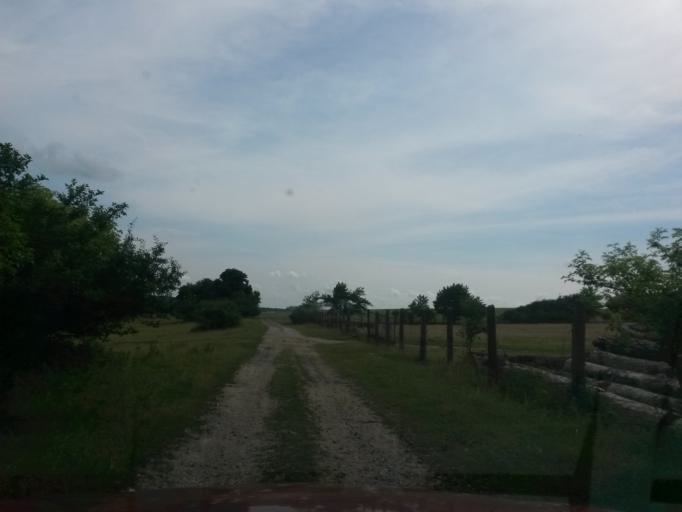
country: SK
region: Kosicky
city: Moldava nad Bodvou
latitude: 48.6691
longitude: 21.1127
